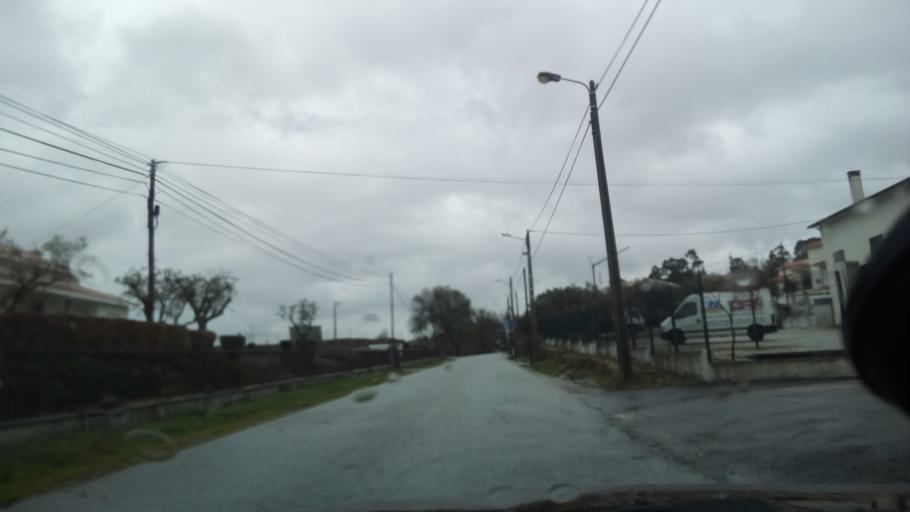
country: PT
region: Guarda
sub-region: Celorico da Beira
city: Celorico da Beira
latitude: 40.6308
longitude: -7.4013
